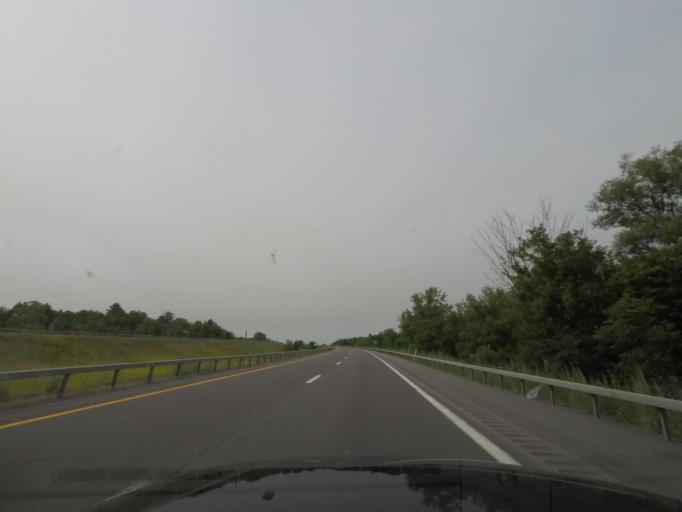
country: US
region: New York
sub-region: Clinton County
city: Champlain
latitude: 44.8803
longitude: -73.4509
